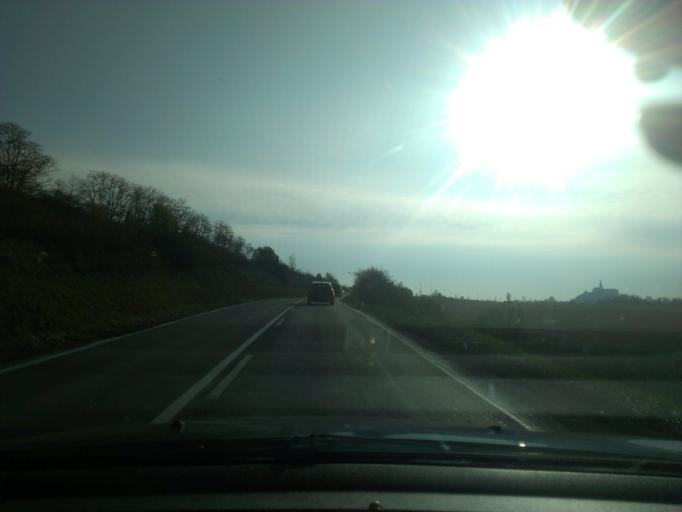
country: SK
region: Nitriansky
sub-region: Okres Nitra
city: Nitra
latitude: 48.3354
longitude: 18.0738
